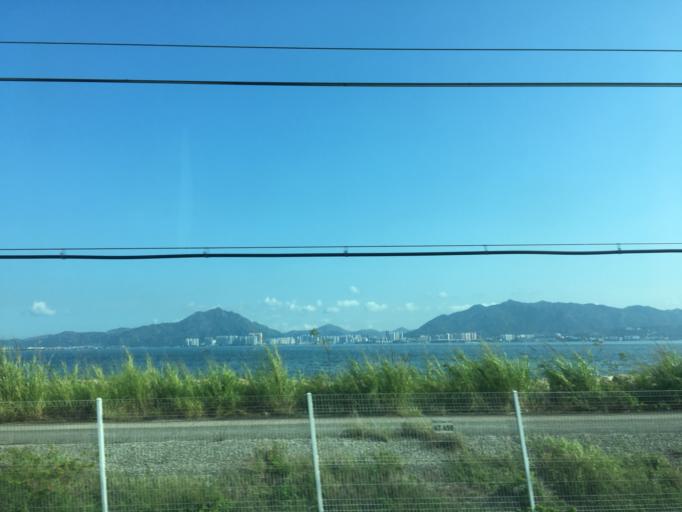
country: HK
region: Tuen Mun
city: Tuen Mun
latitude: 22.3229
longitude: 114.0061
